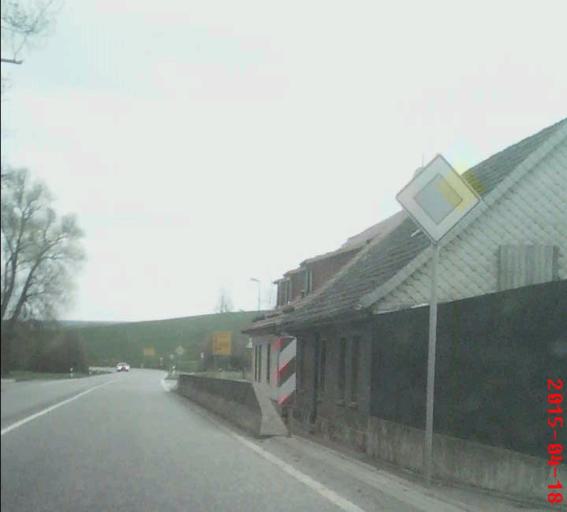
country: DE
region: Thuringia
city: Worbis
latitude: 51.4116
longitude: 10.3784
